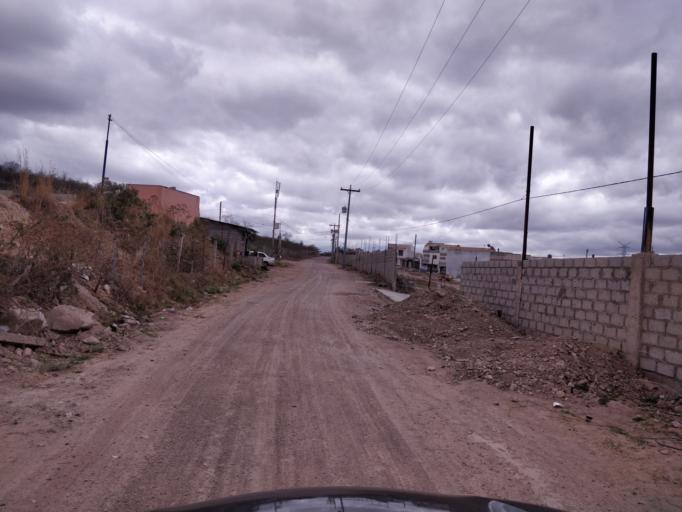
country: HN
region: Francisco Morazan
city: Yaguacire
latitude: 14.0323
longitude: -87.2501
